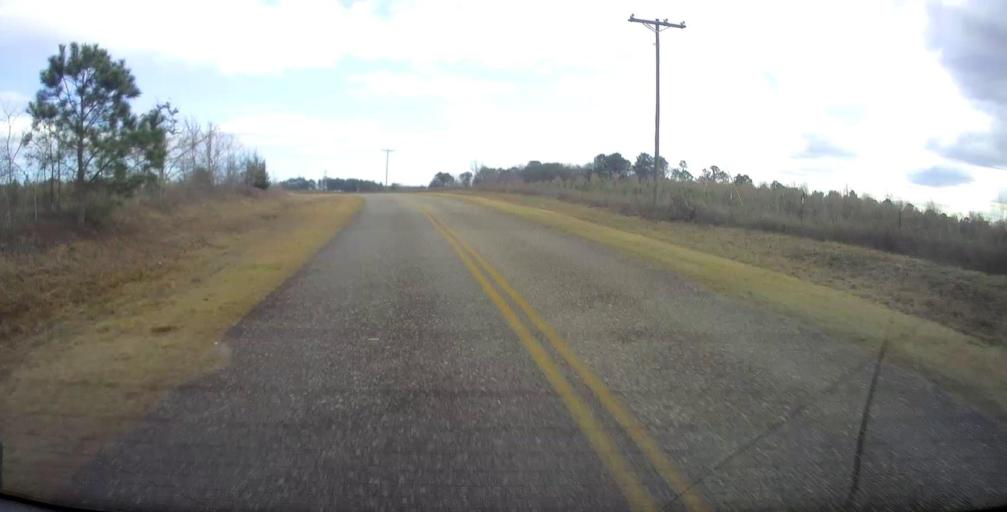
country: US
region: Georgia
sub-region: Marion County
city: Buena Vista
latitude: 32.4136
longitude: -84.4109
